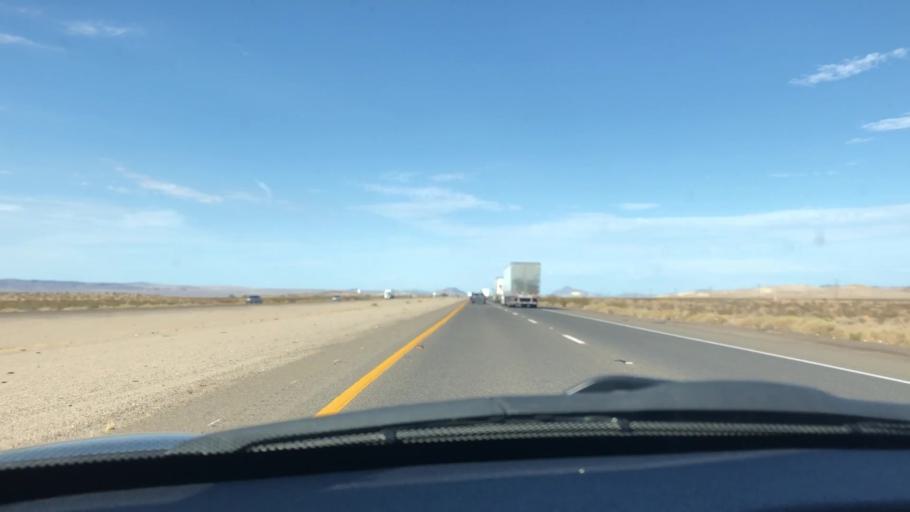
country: US
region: California
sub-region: San Bernardino County
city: Barstow
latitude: 34.9334
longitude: -116.7116
